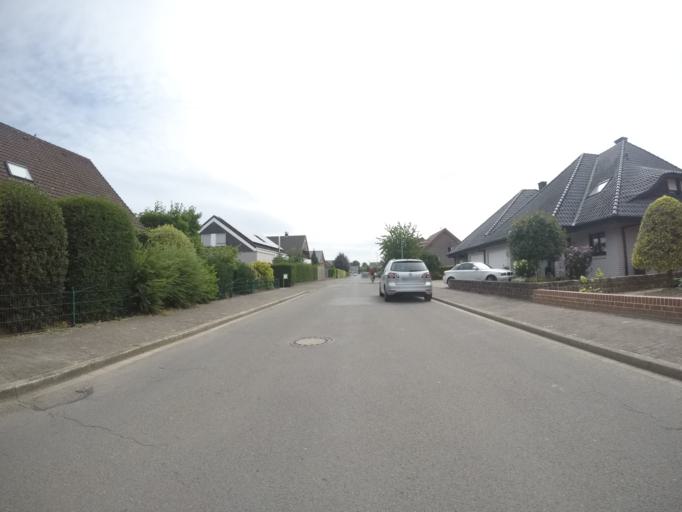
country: DE
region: North Rhine-Westphalia
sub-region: Regierungsbezirk Dusseldorf
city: Bocholt
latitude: 51.8531
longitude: 6.5894
